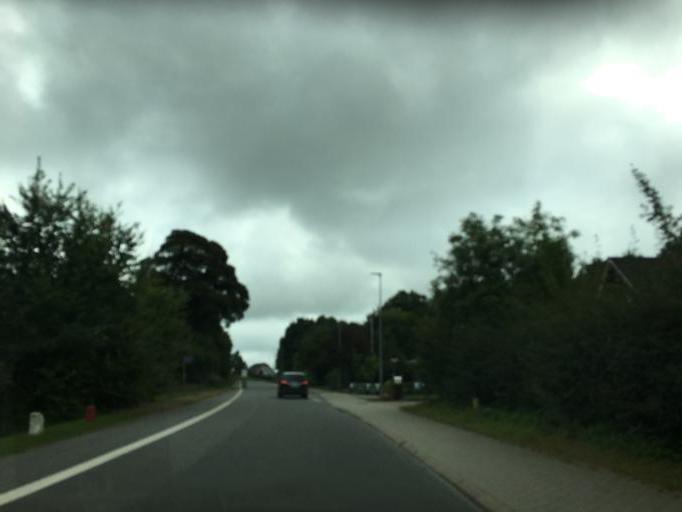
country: DK
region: South Denmark
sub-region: Kolding Kommune
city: Kolding
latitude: 55.5672
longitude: 9.4885
